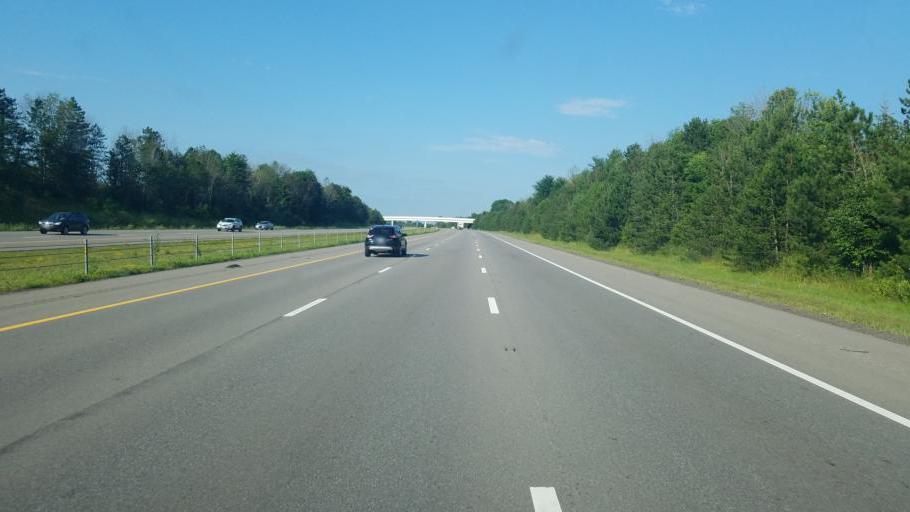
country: US
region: Ohio
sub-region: Morrow County
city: Cardington
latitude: 40.4409
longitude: -82.8037
